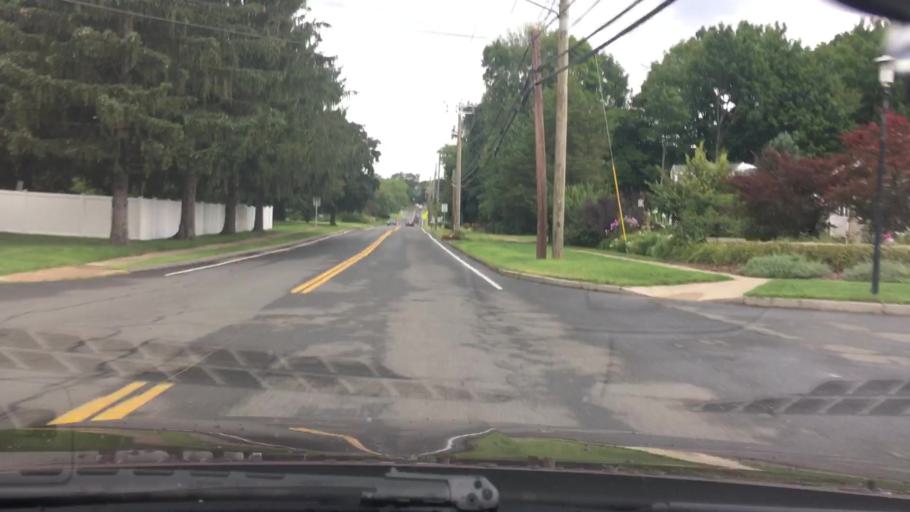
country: US
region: Connecticut
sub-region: Hartford County
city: Manchester
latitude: 41.7535
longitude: -72.5407
